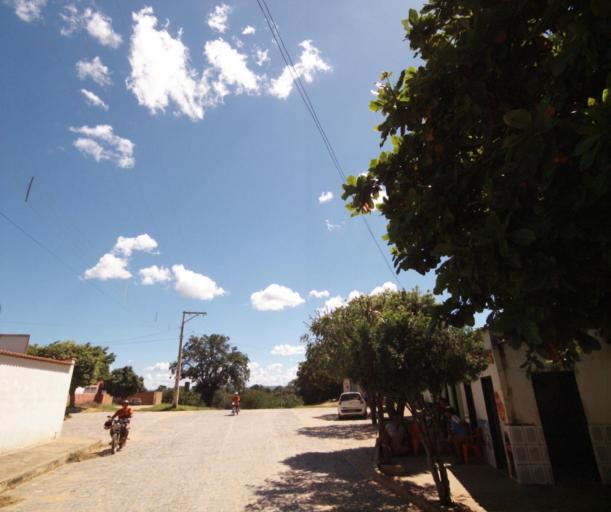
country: BR
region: Bahia
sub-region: Carinhanha
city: Carinhanha
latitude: -14.2142
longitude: -44.2838
